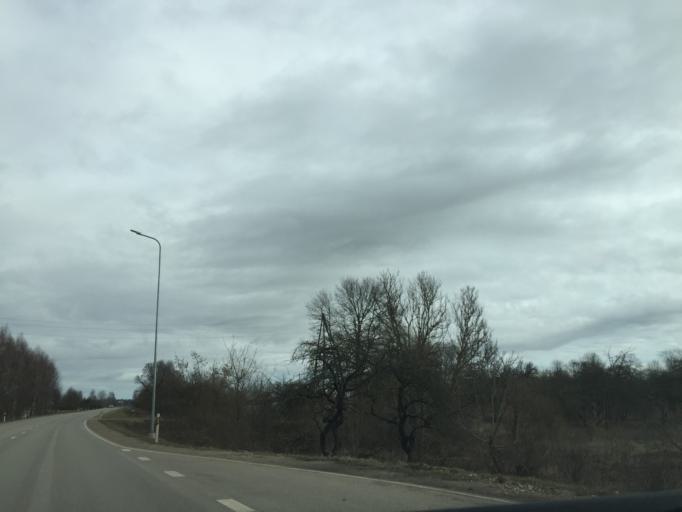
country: LV
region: Daugavpils
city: Daugavpils
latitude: 55.9111
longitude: 26.6583
